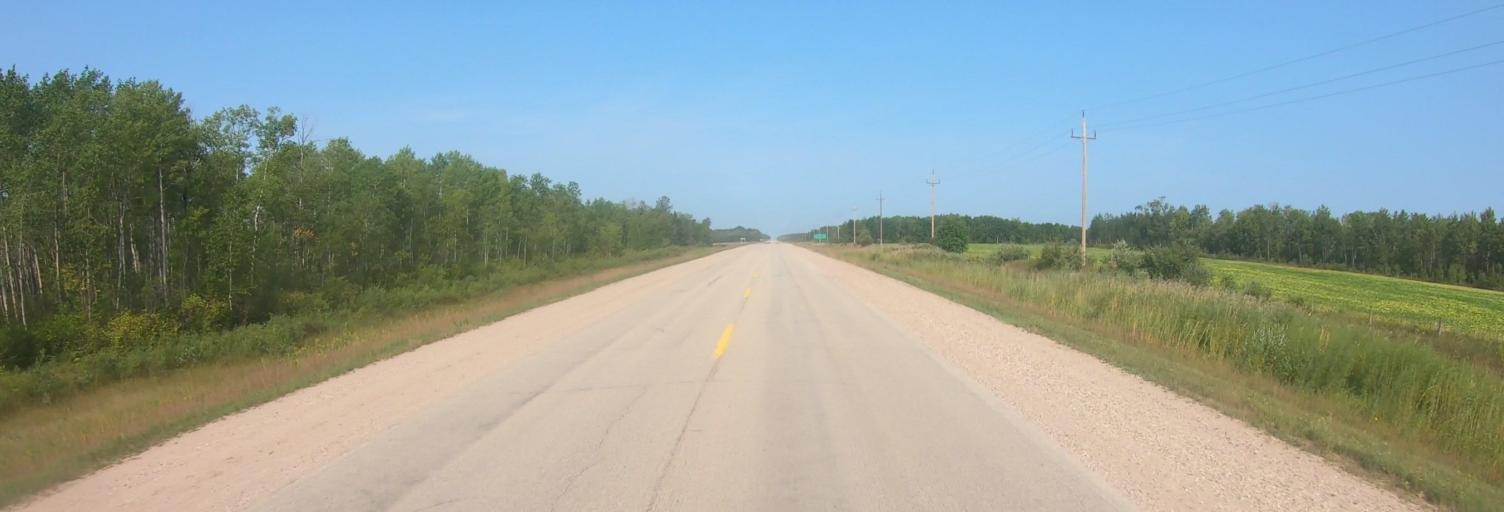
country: US
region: Minnesota
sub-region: Roseau County
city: Roseau
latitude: 49.0922
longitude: -95.9860
